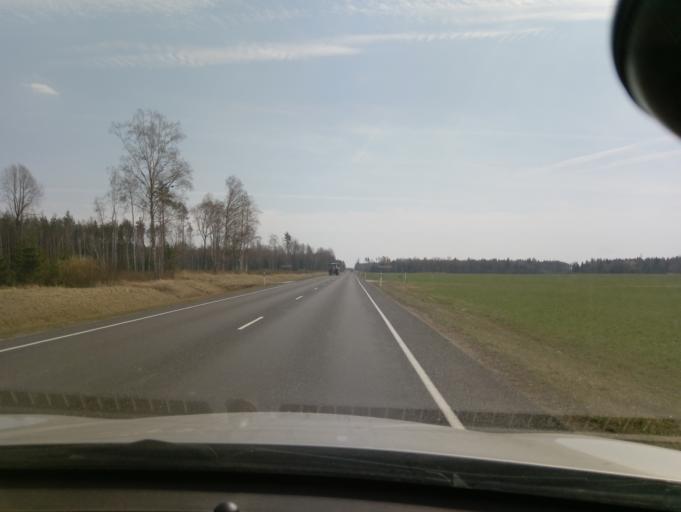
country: EE
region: Viljandimaa
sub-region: Vohma linn
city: Vohma
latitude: 58.7262
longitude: 25.5994
